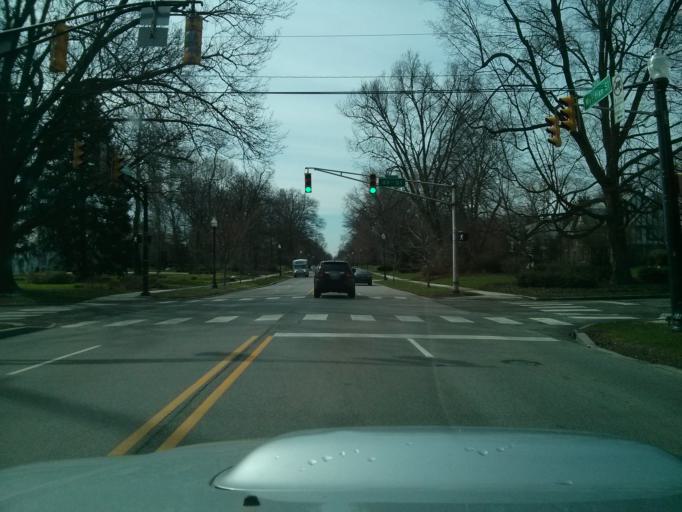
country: US
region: Indiana
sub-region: Marion County
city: Broad Ripple
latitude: 39.8429
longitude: -86.1570
